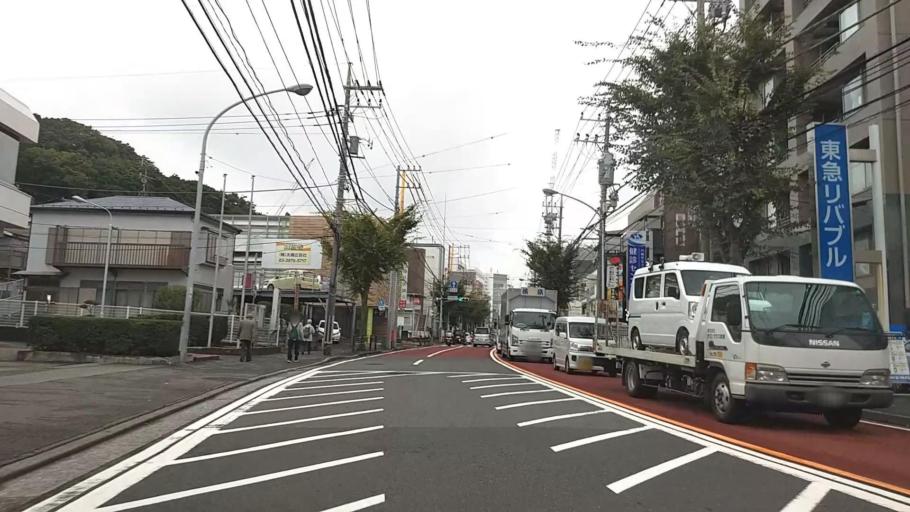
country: JP
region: Kanagawa
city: Fujisawa
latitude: 35.3978
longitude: 139.5307
